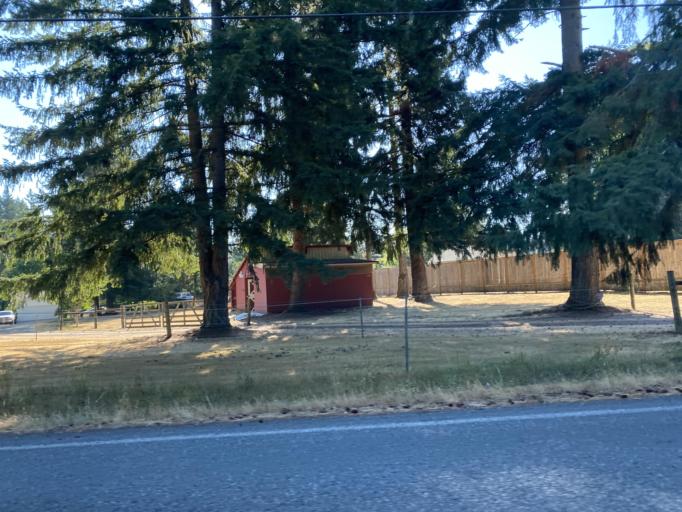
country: US
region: Washington
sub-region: Thurston County
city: Tanglewilde-Thompson Place
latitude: 46.9882
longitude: -122.7388
